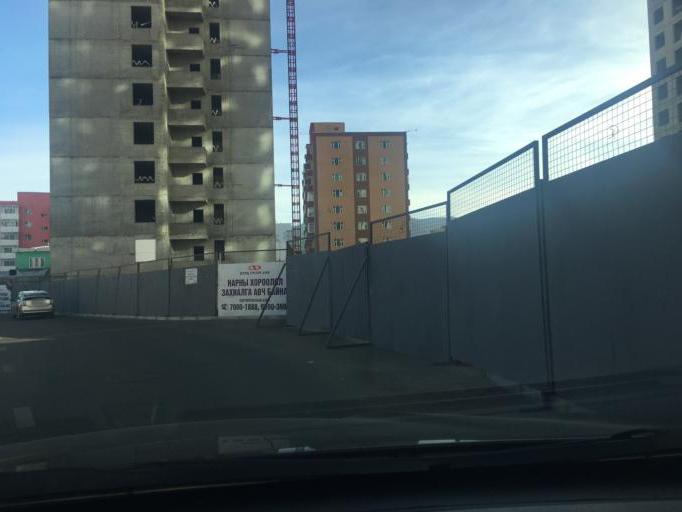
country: MN
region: Ulaanbaatar
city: Ulaanbaatar
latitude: 47.9044
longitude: 106.8969
